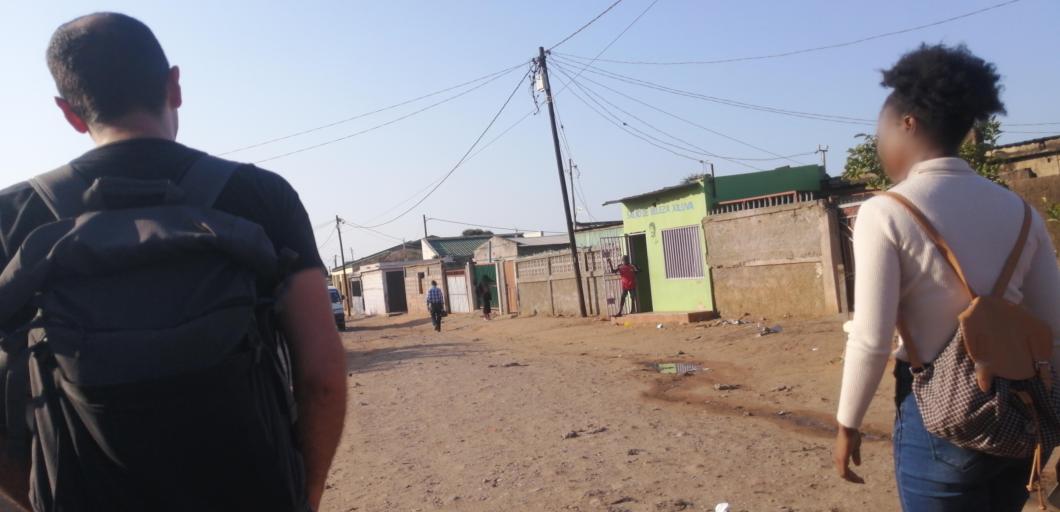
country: MZ
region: Maputo City
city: Maputo
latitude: -25.9536
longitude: 32.5691
